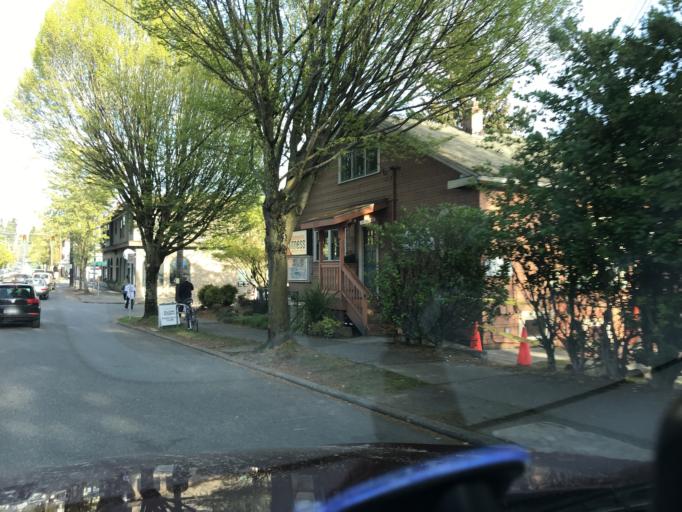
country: US
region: Washington
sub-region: King County
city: Seattle
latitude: 47.6758
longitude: -122.3051
